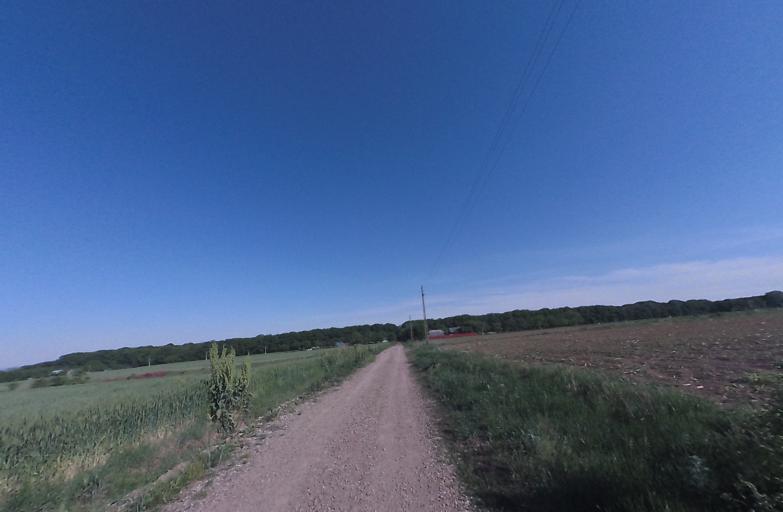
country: RO
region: Neamt
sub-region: Comuna Dulcesti
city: Dulcesti
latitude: 46.9988
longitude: 26.7803
